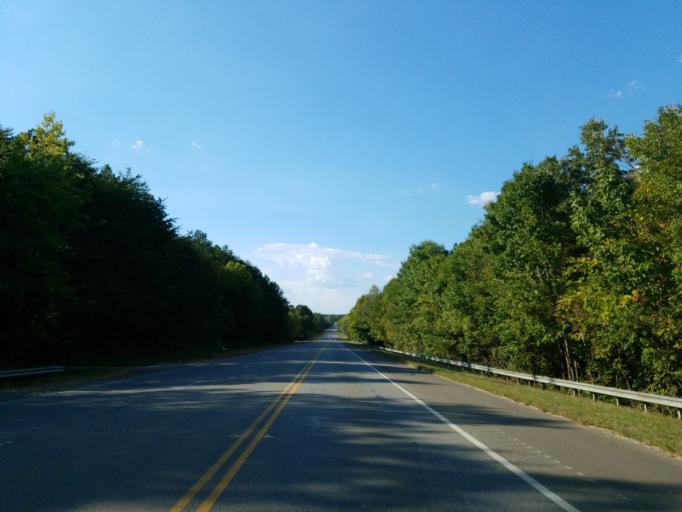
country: US
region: Georgia
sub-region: Murray County
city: Chatsworth
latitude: 34.6877
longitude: -84.7315
